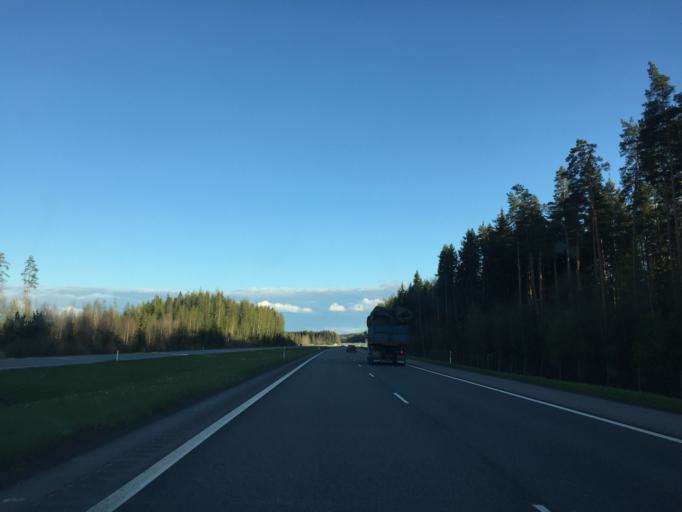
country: FI
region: Haeme
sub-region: Riihimaeki
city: Riihimaeki
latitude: 60.7773
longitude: 24.7112
